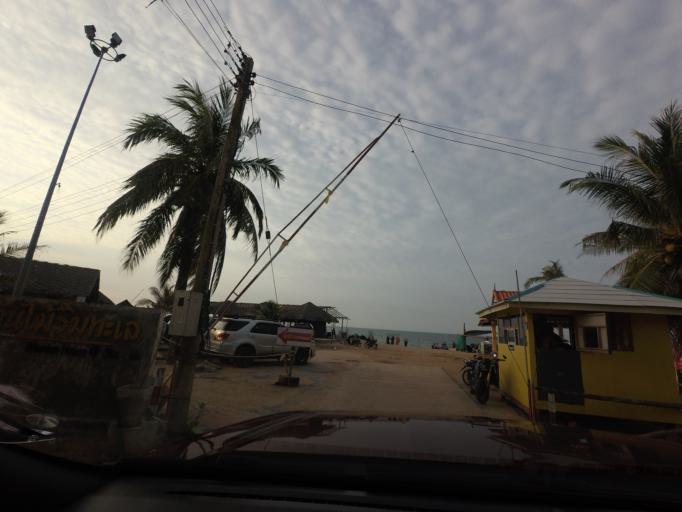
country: TH
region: Pattani
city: Yaring
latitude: 6.9301
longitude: 101.3223
